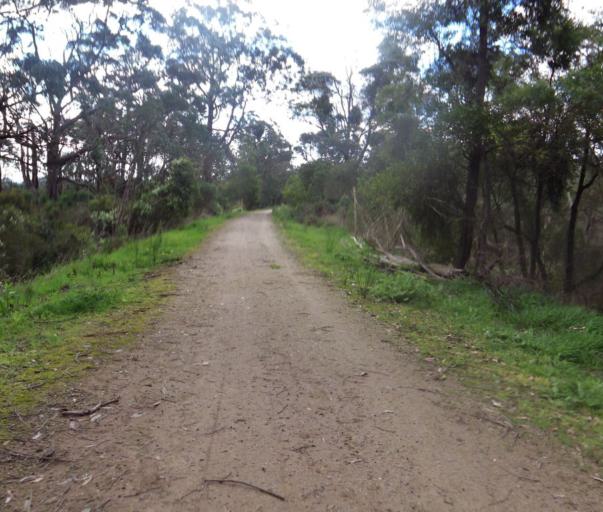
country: AU
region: Victoria
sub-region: Bass Coast
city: North Wonthaggi
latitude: -38.6637
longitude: 146.0243
